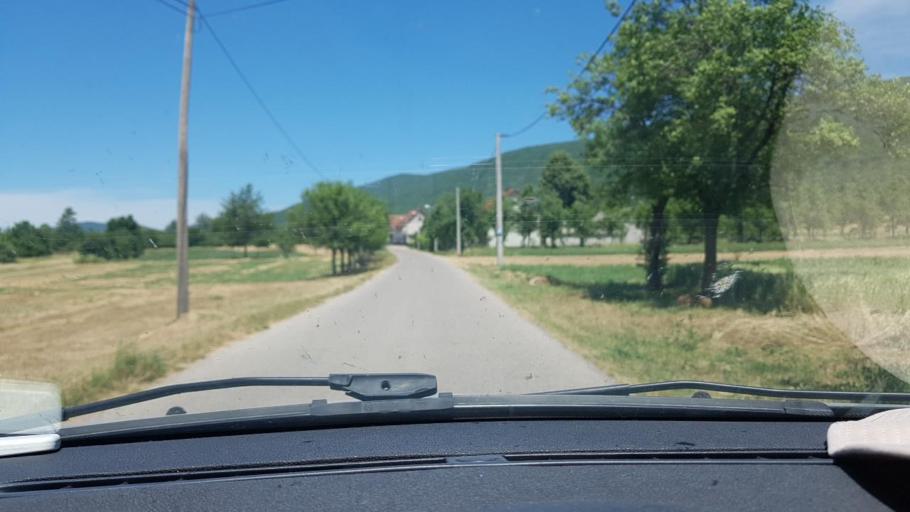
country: HR
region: Licko-Senjska
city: Otocac
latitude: 44.7980
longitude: 15.3644
